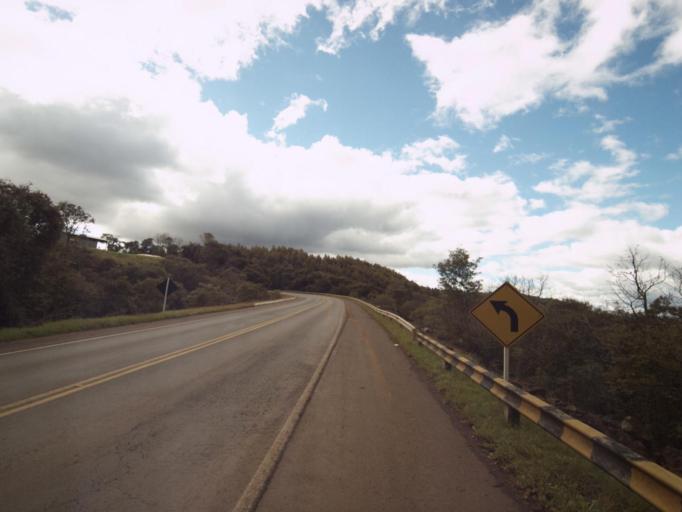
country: BR
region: Santa Catarina
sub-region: Concordia
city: Concordia
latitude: -27.2923
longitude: -51.9689
